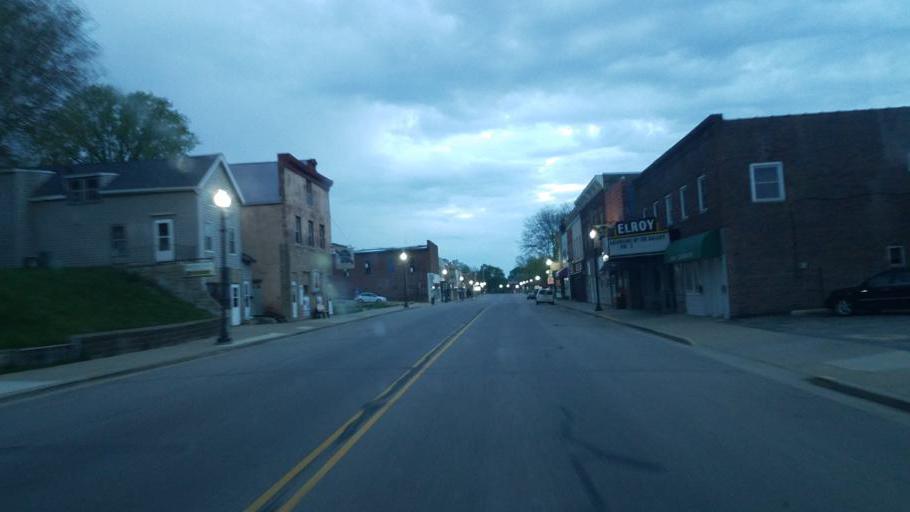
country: US
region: Wisconsin
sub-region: Juneau County
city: Elroy
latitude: 43.7374
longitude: -90.2693
